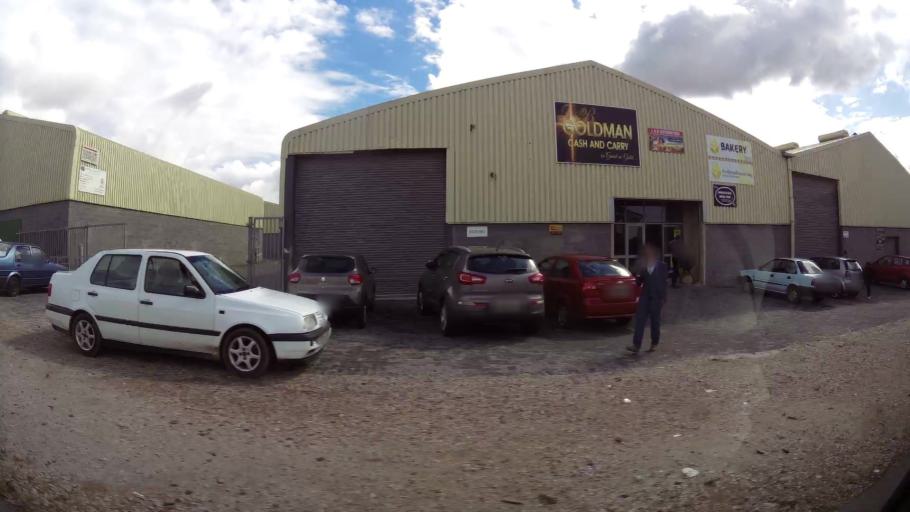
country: ZA
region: Eastern Cape
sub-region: Nelson Mandela Bay Metropolitan Municipality
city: Port Elizabeth
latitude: -33.9269
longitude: 25.5667
